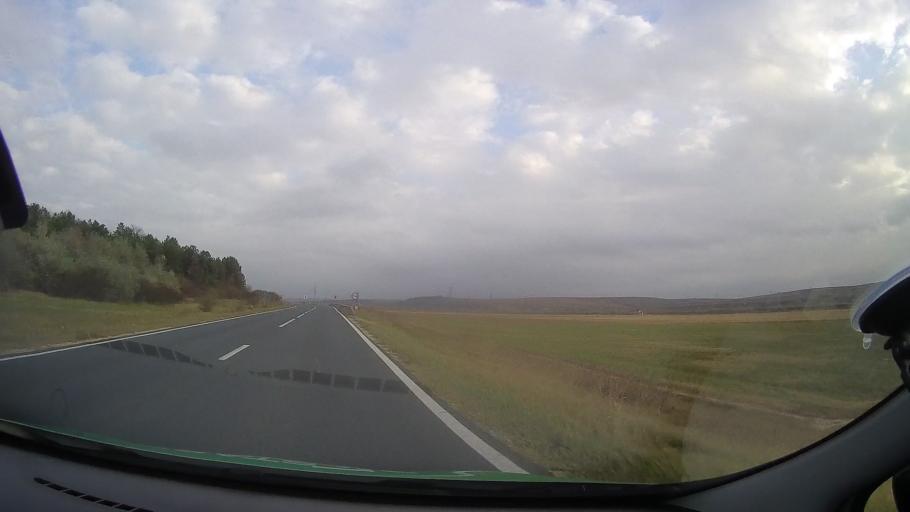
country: RO
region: Constanta
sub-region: Comuna Mircea Voda
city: Mircea Voda
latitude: 44.2684
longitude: 28.1796
